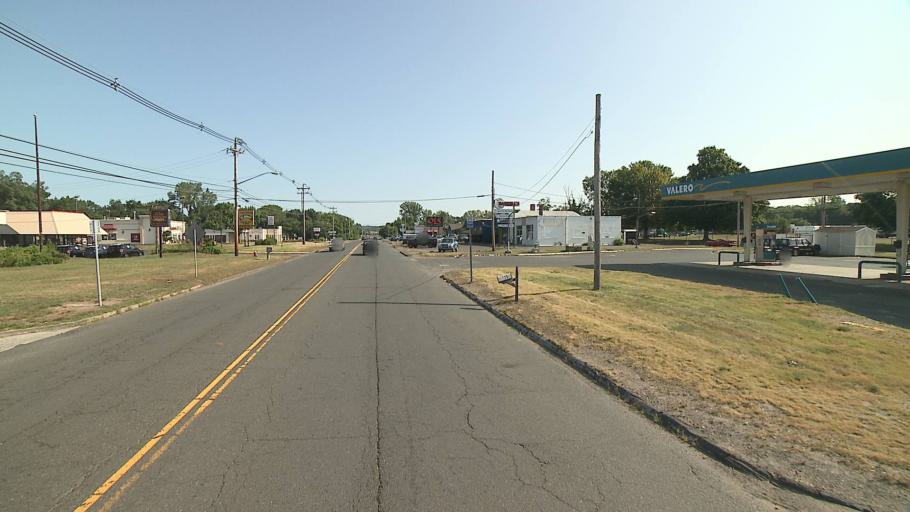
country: US
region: Connecticut
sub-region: New Haven County
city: Wallingford
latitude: 41.4729
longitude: -72.8148
